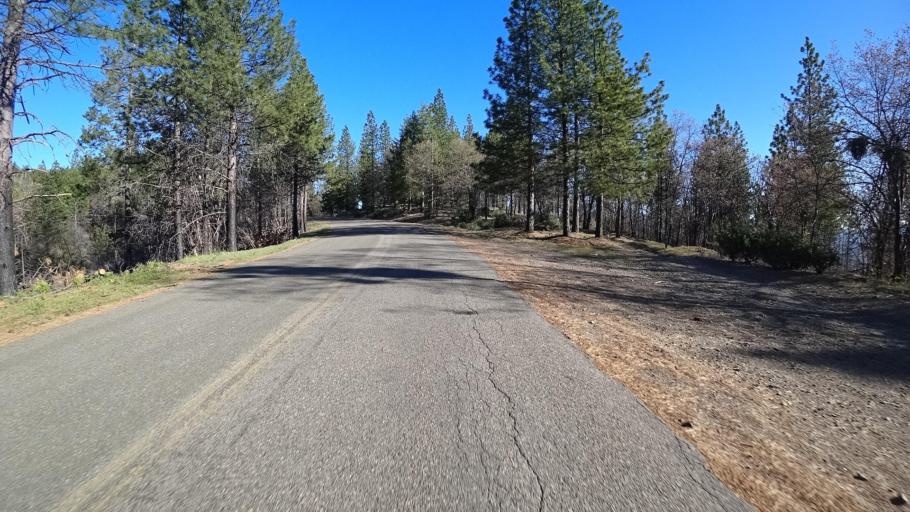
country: US
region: California
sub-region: Lake County
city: Upper Lake
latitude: 39.3117
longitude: -122.9427
